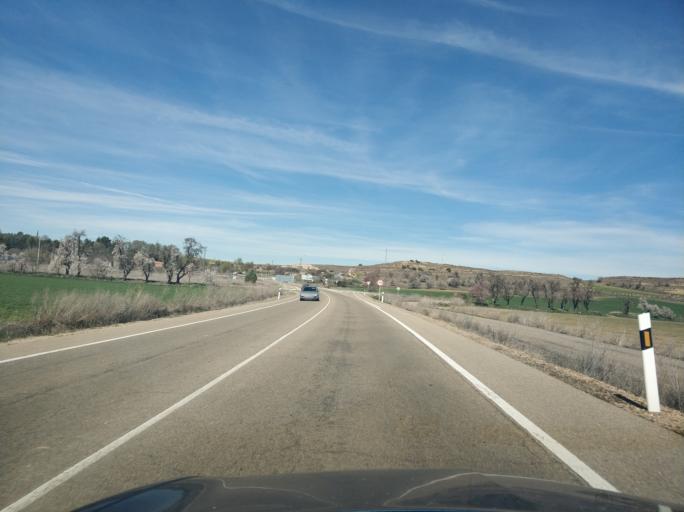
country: ES
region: Castille and Leon
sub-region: Provincia de Valladolid
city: Simancas
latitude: 41.5925
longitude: -4.8182
